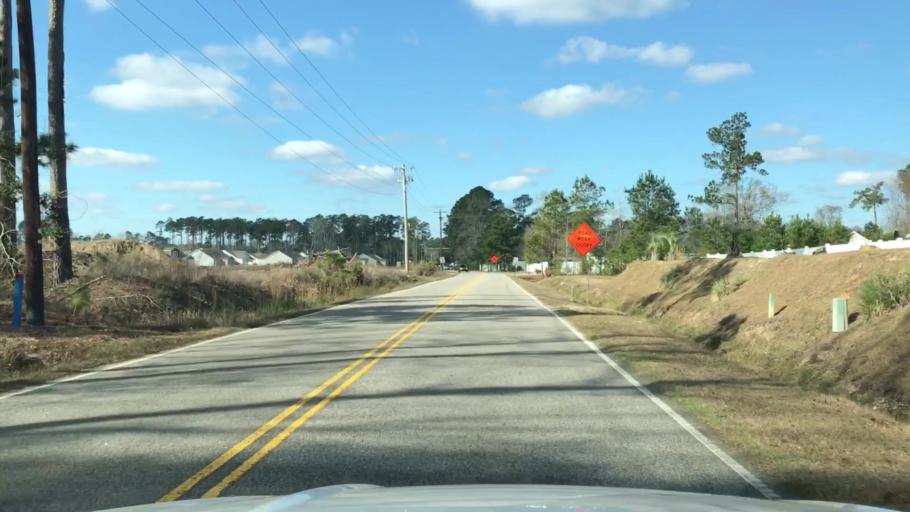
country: US
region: South Carolina
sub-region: Horry County
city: Socastee
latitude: 33.6591
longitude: -79.0058
